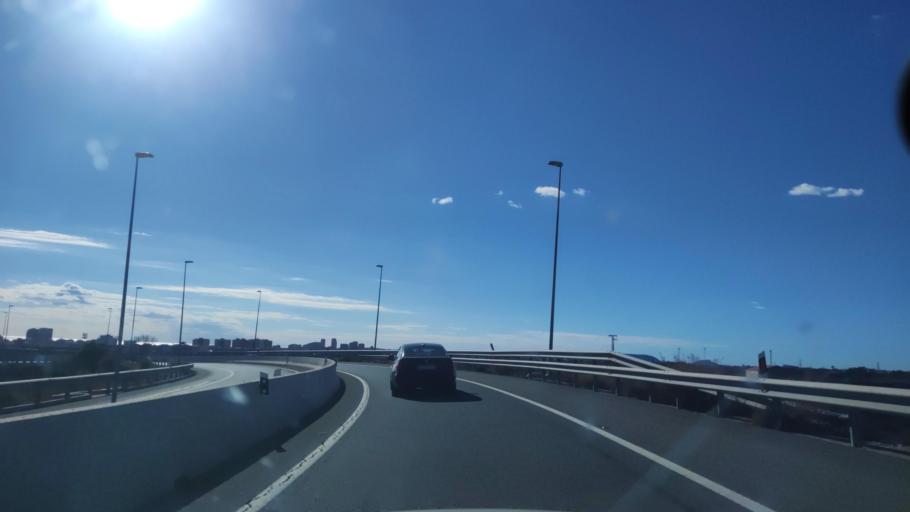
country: ES
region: Valencia
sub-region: Provincia de Alicante
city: el Campello
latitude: 38.4401
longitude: -0.4055
